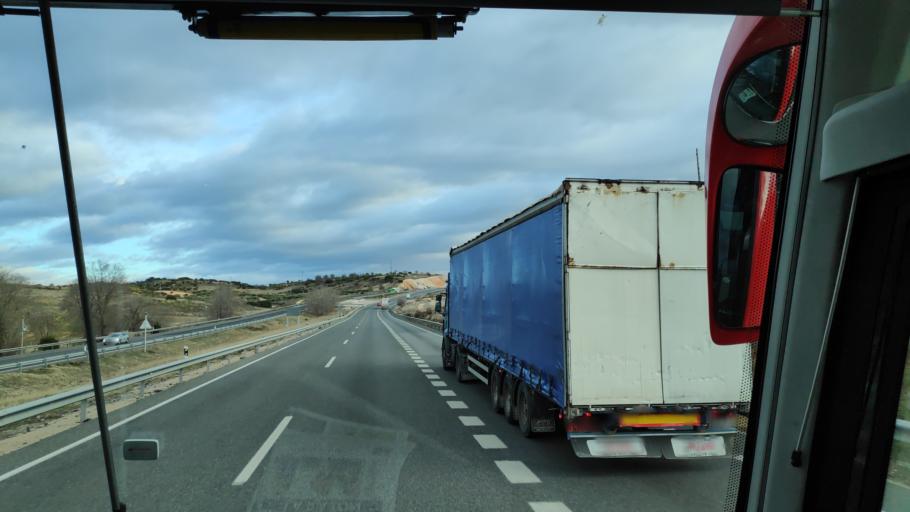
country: ES
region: Madrid
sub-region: Provincia de Madrid
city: Villarejo de Salvanes
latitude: 40.1960
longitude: -3.3058
